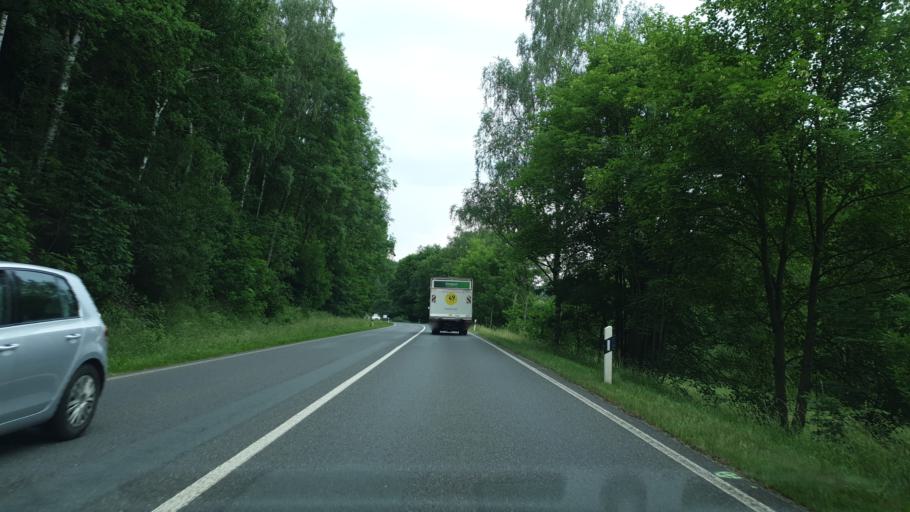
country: DE
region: Saxony
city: Lengenfeld
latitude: 50.5601
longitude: 12.3821
